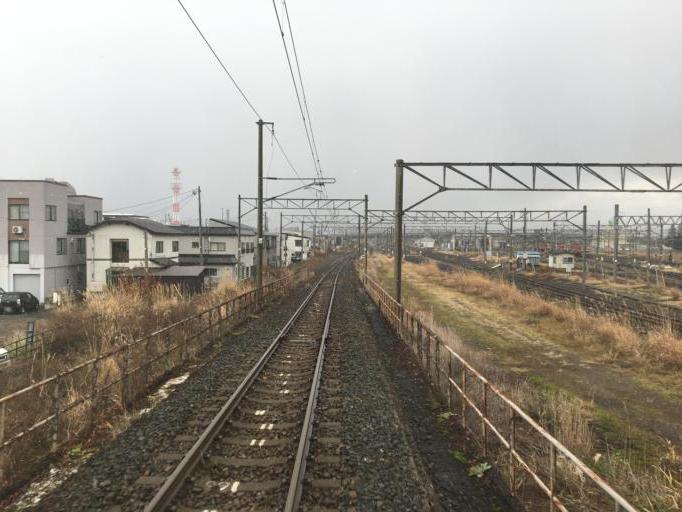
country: JP
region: Aomori
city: Aomori Shi
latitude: 40.8193
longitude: 140.7374
